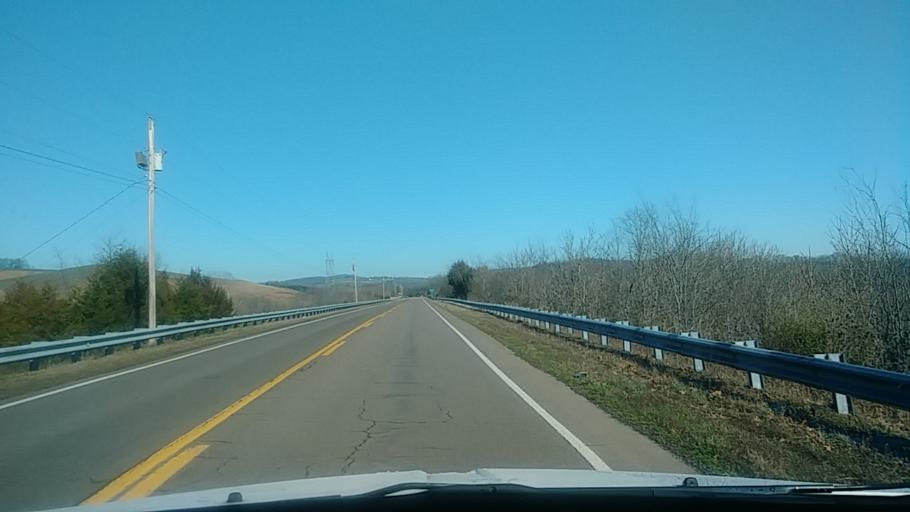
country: US
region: Tennessee
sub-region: Hamblen County
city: Morristown
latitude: 36.1833
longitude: -83.1667
